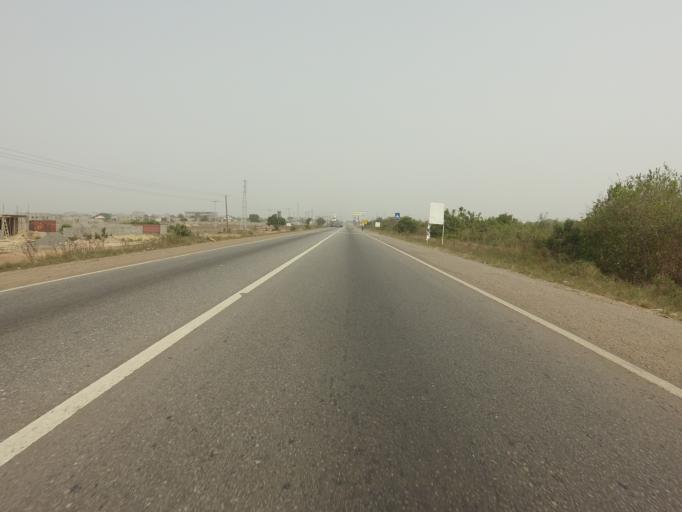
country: GH
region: Greater Accra
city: Tema
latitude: 5.7745
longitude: 0.0792
